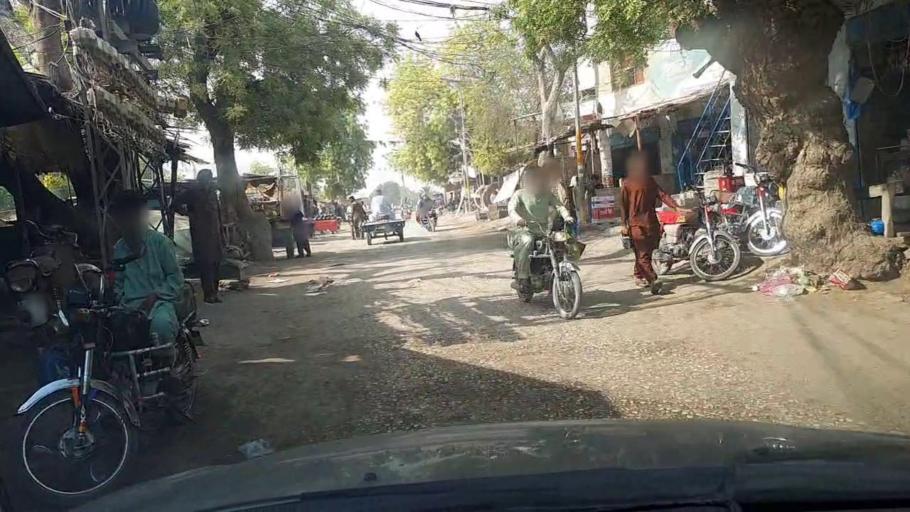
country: PK
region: Sindh
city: Mirpur Mathelo
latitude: 28.0199
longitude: 69.5511
